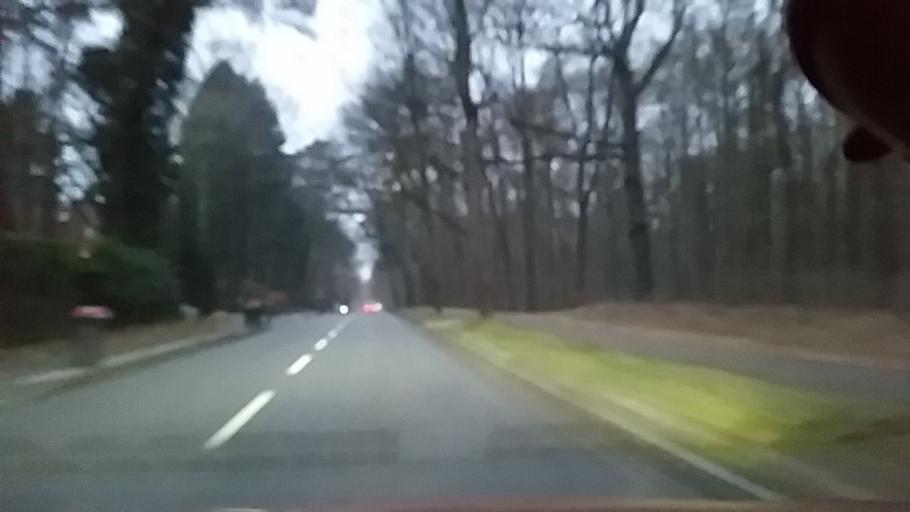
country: DE
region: Schleswig-Holstein
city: Wedel
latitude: 53.5754
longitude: 9.7792
